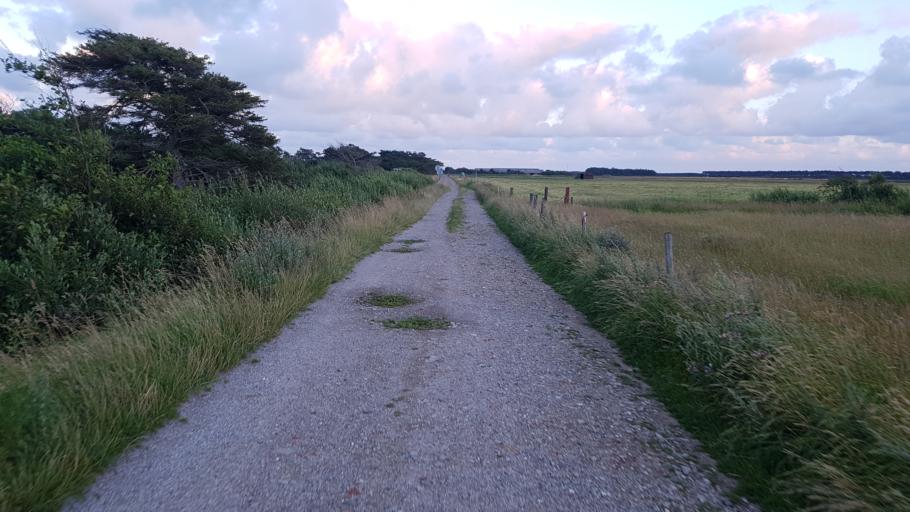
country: DE
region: Schleswig-Holstein
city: List
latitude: 55.1073
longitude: 8.5068
